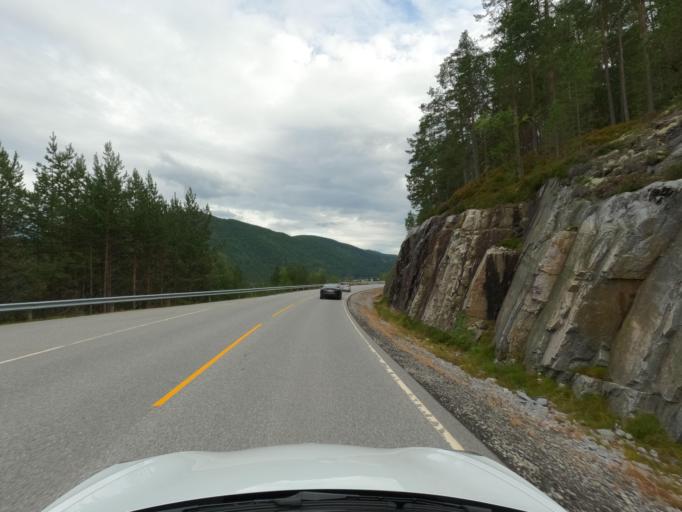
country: NO
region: Telemark
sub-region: Hjartdal
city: Sauland
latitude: 59.7692
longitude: 9.0171
